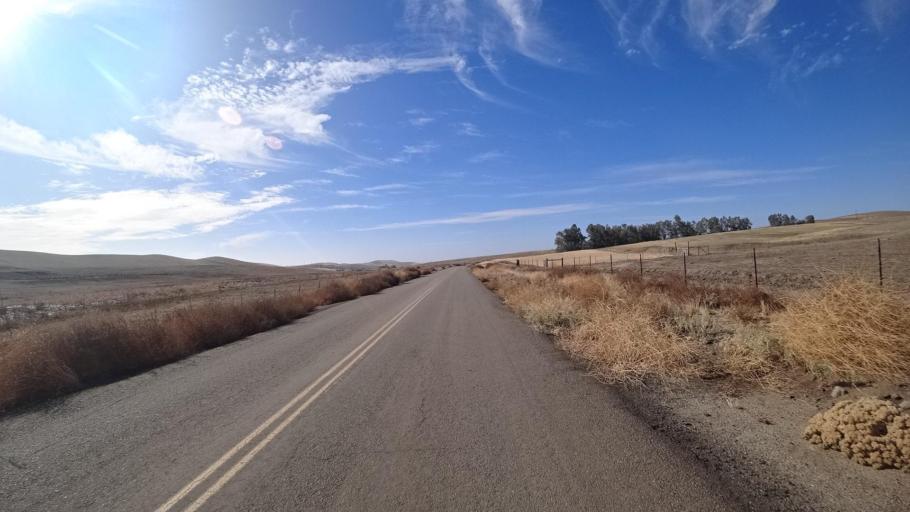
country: US
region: California
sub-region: Tulare County
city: Richgrove
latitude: 35.6312
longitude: -118.9662
